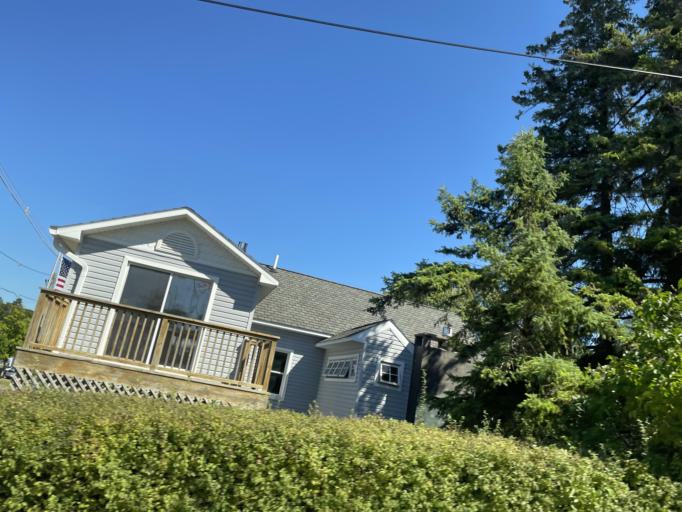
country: US
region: Michigan
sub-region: Charlevoix County
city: Charlevoix
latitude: 45.3186
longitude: -85.2641
